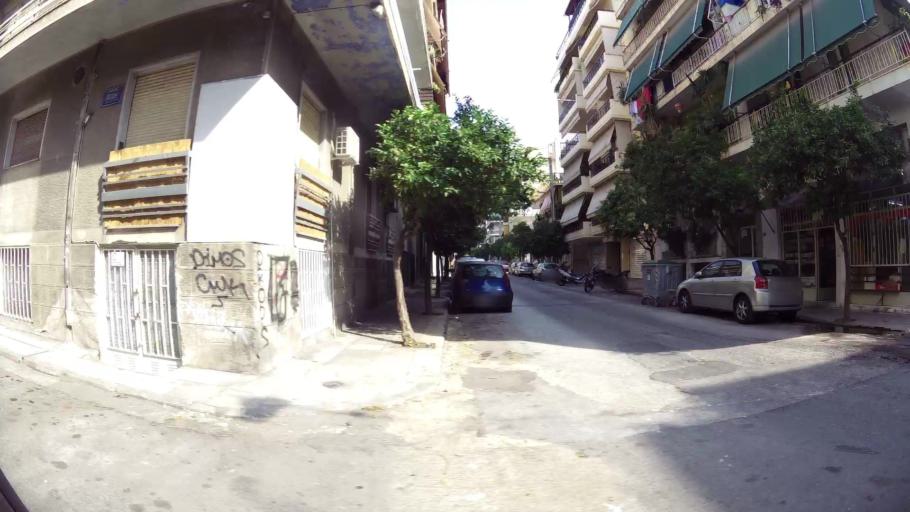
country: GR
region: Attica
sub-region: Nomarchia Athinas
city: Athens
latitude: 37.9915
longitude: 23.7161
